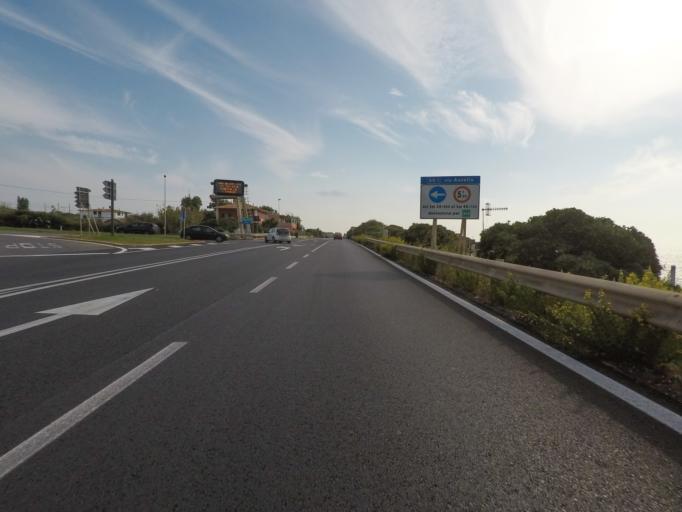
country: IT
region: Latium
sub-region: Citta metropolitana di Roma Capitale
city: Civitavecchia
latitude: 42.0556
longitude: 11.8198
